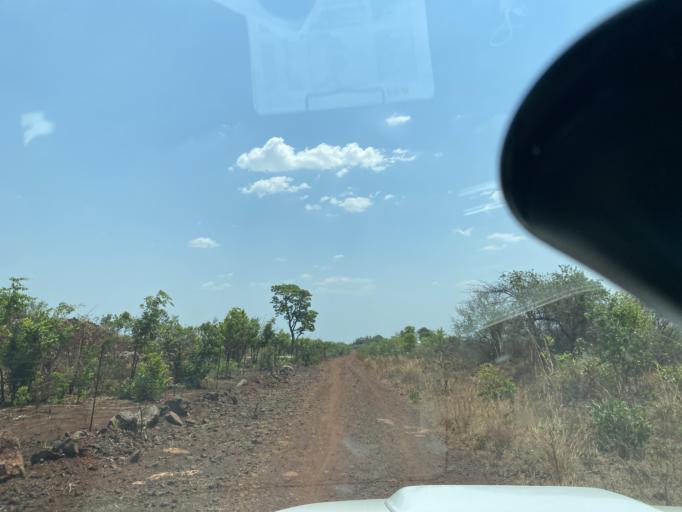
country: ZM
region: Lusaka
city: Lusaka
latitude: -15.4976
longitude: 27.9680
